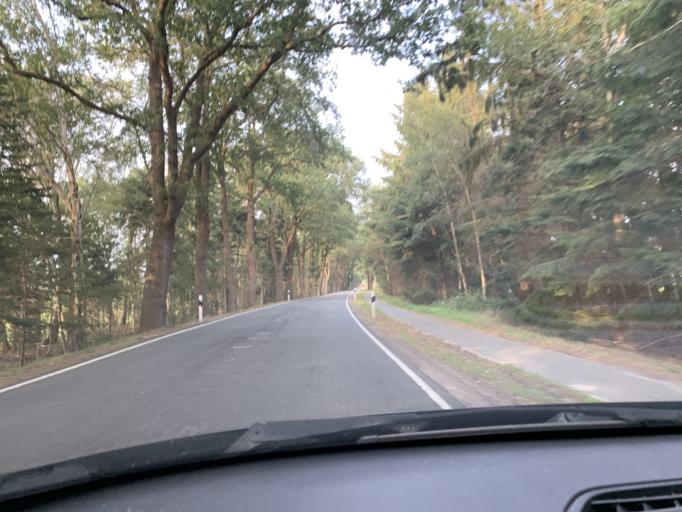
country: DE
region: Lower Saxony
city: Apen
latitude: 53.1948
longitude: 7.7878
